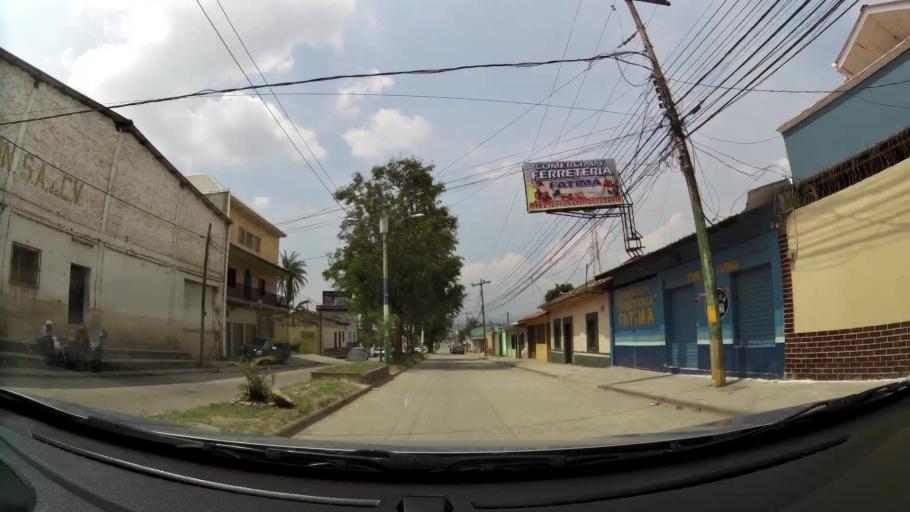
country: HN
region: Comayagua
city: Siguatepeque
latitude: 14.6059
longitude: -87.8306
